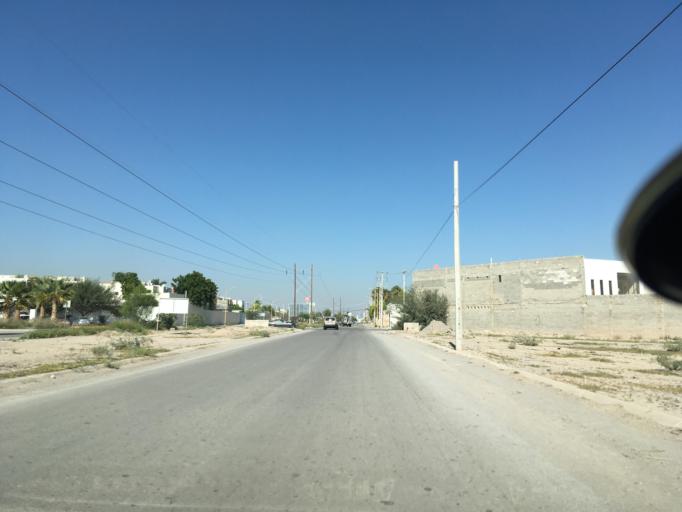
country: MX
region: Coahuila
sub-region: Torreon
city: Fraccionamiento la Noria
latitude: 25.5744
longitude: -103.3731
